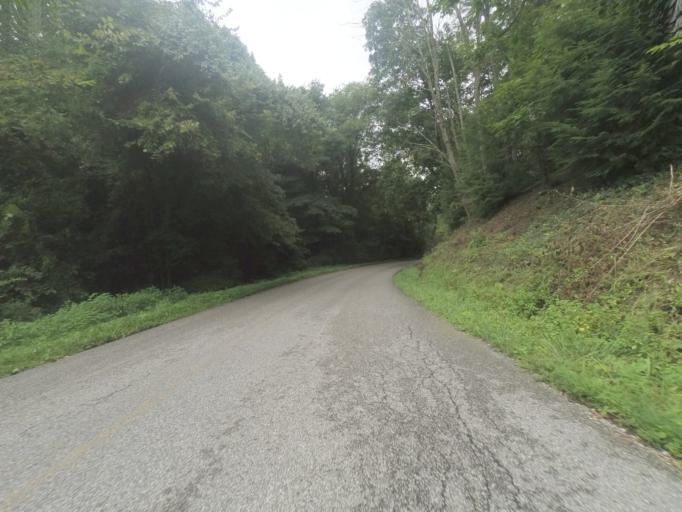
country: US
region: West Virginia
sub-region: Cabell County
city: Huntington
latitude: 38.4296
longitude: -82.4689
